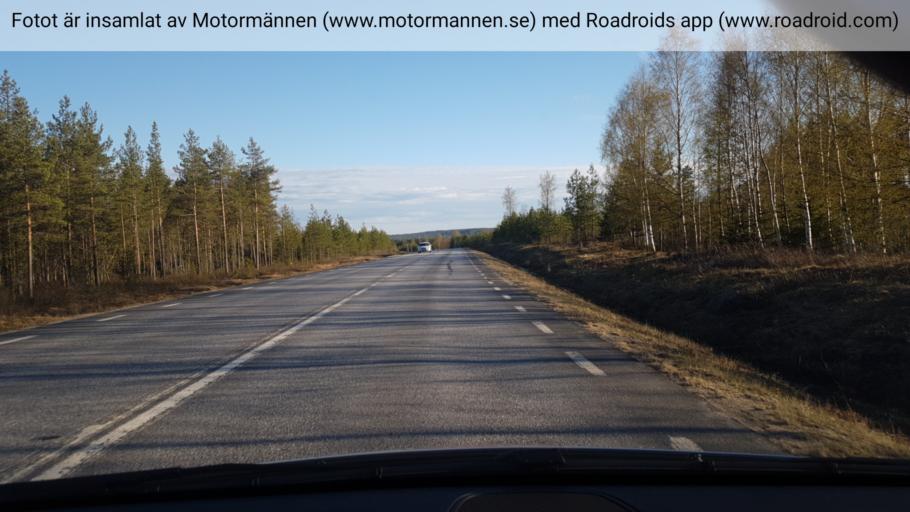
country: SE
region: Vaesterbotten
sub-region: Vannas Kommun
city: Vaennaes
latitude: 63.9882
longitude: 19.7316
